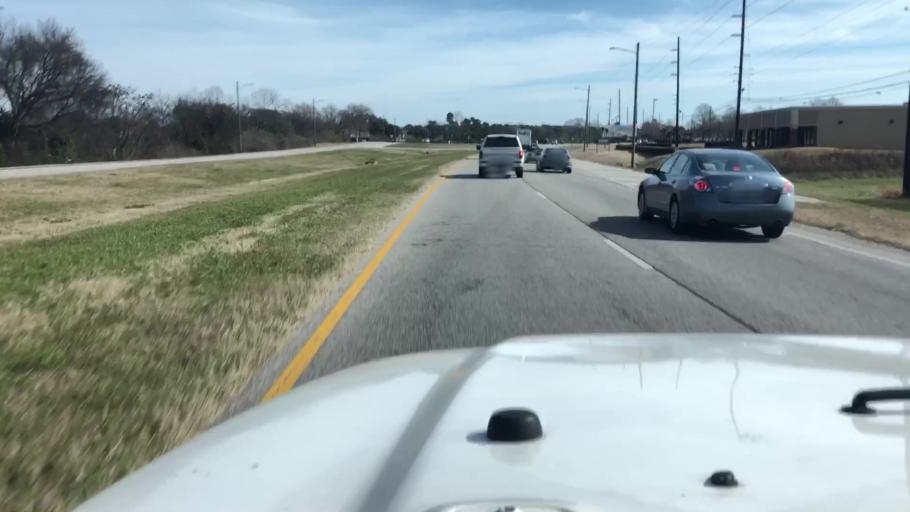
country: US
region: Alabama
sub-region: Elmore County
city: Blue Ridge
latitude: 32.3823
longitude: -86.1662
